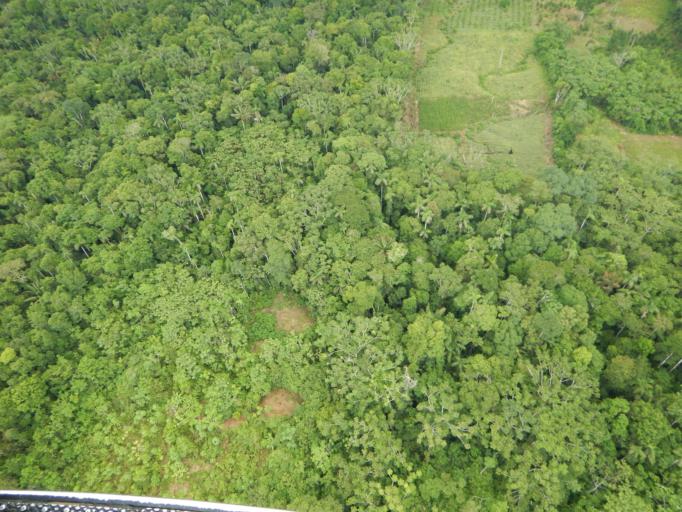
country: BO
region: Cochabamba
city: Chimore
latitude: -17.1408
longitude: -64.7087
